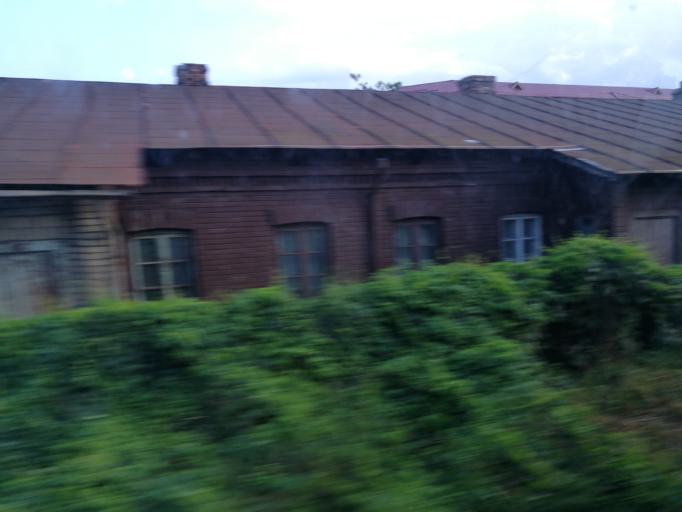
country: RO
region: Dambovita
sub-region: Comuna Titu
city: Salcuta
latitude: 44.6619
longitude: 25.5714
